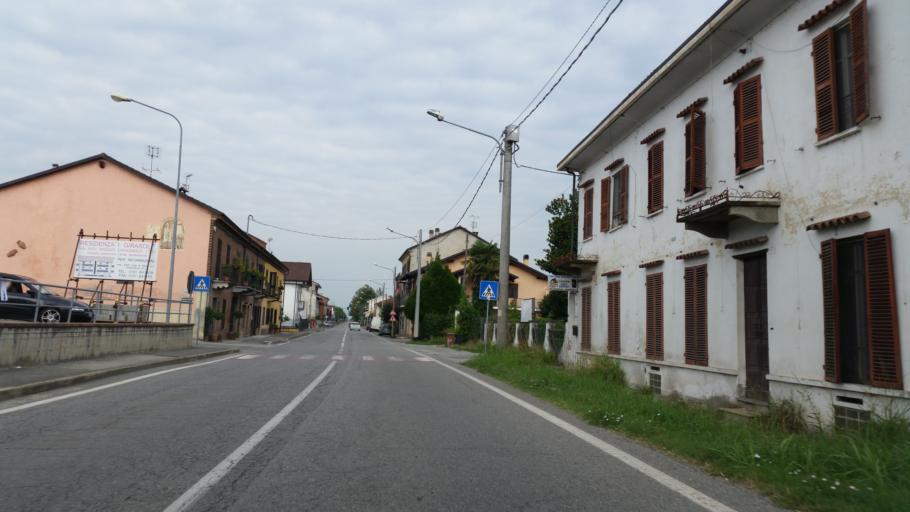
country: IT
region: Piedmont
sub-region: Provincia di Torino
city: Pomaretto
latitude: 45.1562
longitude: 8.0472
